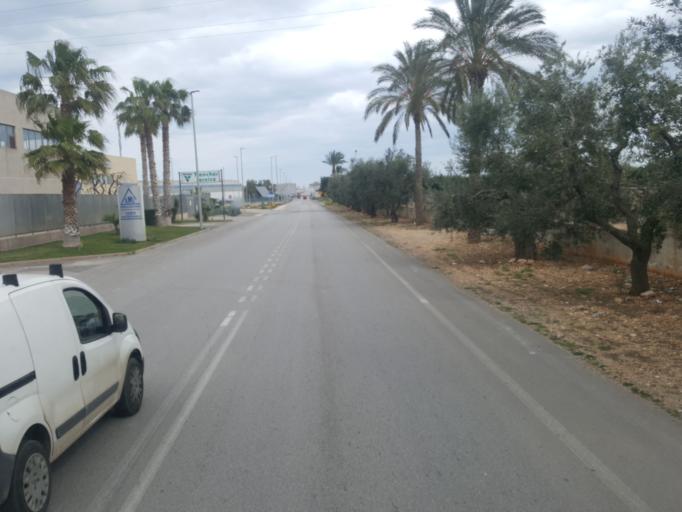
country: IT
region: Apulia
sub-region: Provincia di Bari
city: Modugno
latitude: 41.0996
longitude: 16.7877
